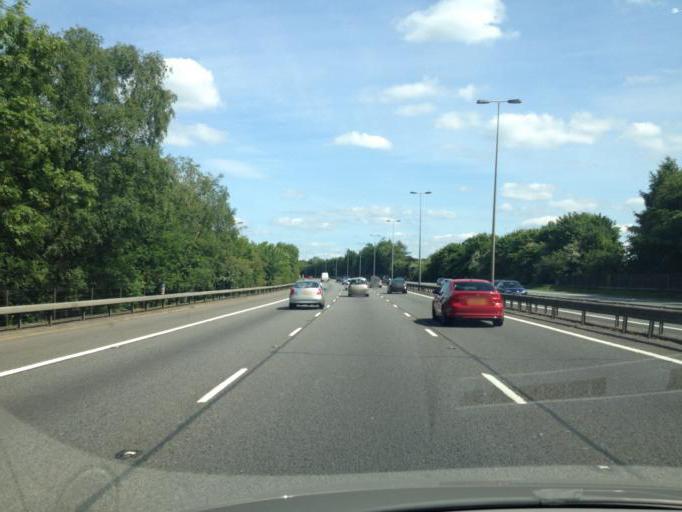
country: GB
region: England
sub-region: Buckinghamshire
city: Stokenchurch
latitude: 51.6286
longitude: -0.8671
